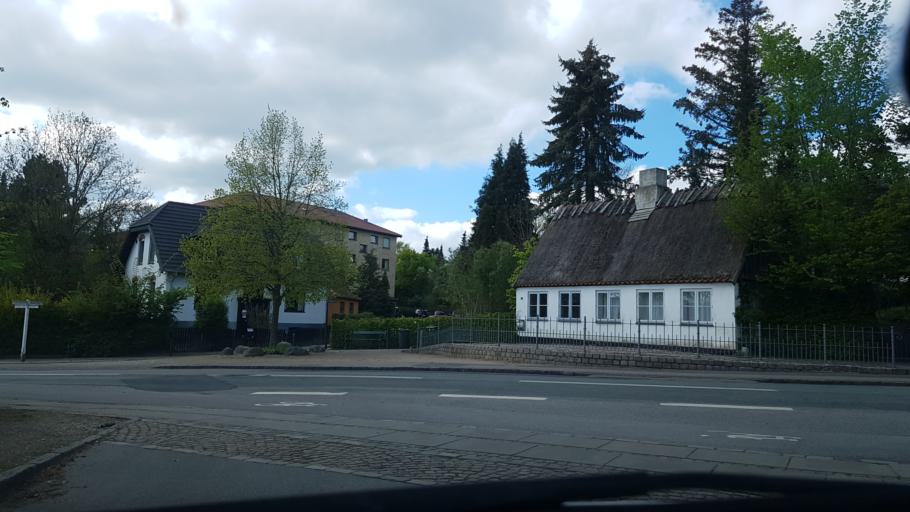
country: DK
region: Capital Region
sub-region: Rudersdal Kommune
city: Holte
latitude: 55.8170
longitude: 12.4887
